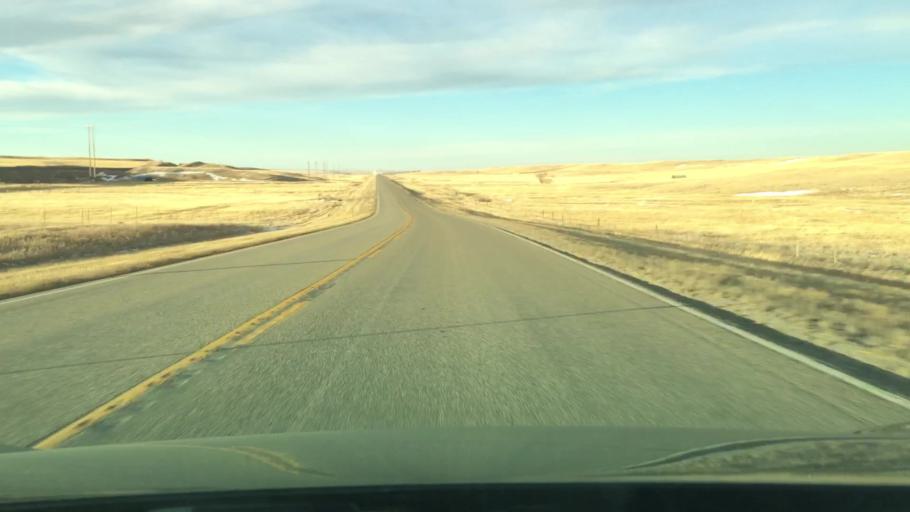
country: US
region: Montana
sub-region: Wheatland County
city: Harlowton
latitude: 46.7111
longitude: -109.7361
